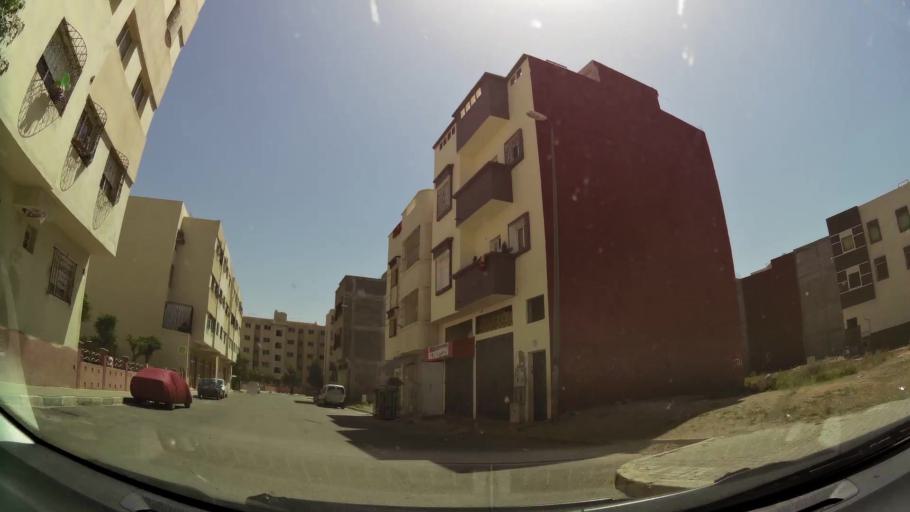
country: MA
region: Souss-Massa-Draa
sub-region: Inezgane-Ait Mellou
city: Inezgane
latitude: 30.3427
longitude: -9.5145
